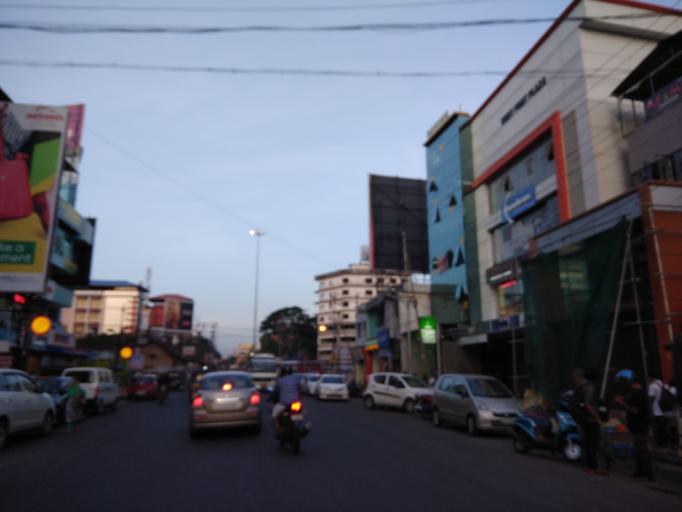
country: IN
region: Kerala
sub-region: Thrissur District
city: Trichur
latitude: 10.5222
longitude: 76.2012
